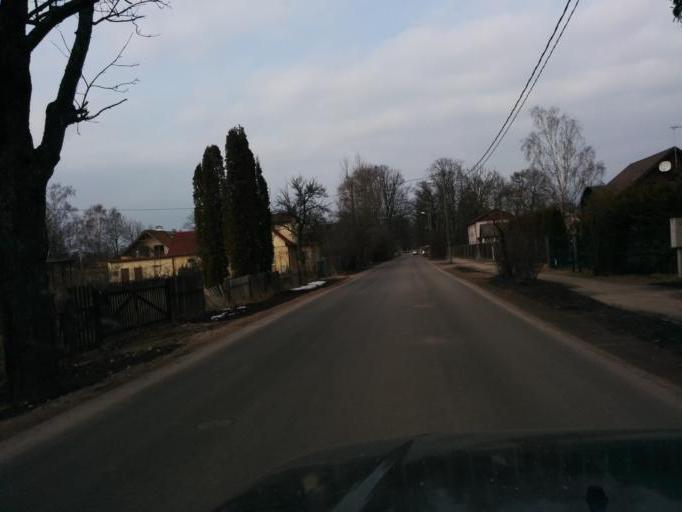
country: LV
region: Jurmala
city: Jurmala
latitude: 56.9572
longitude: 23.7234
